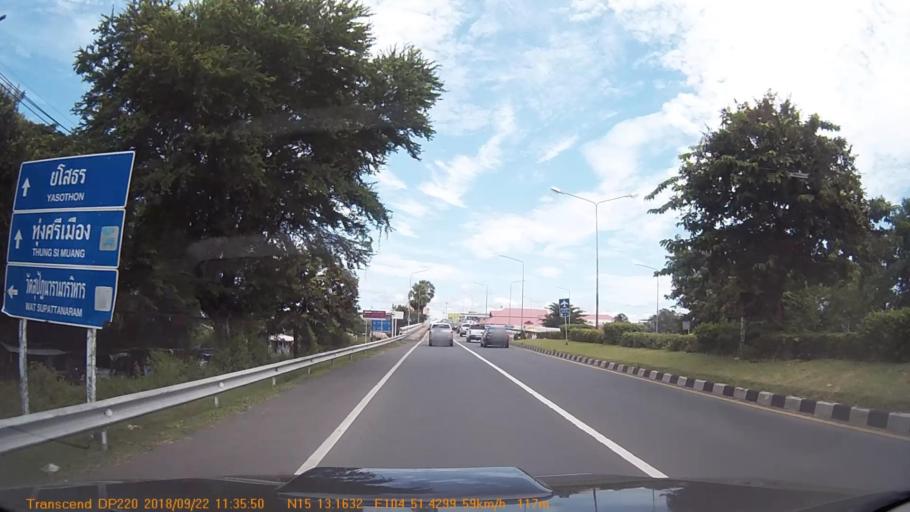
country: TH
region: Changwat Ubon Ratchathani
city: Ubon Ratchathani
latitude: 15.2196
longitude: 104.8572
